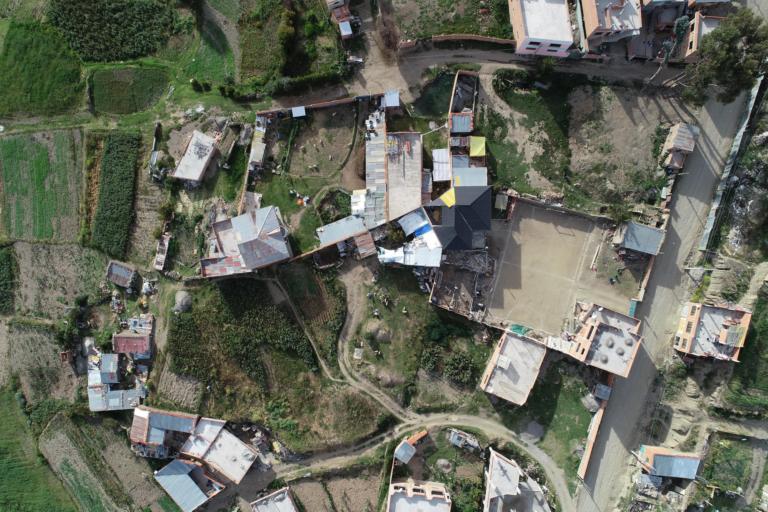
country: BO
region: La Paz
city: La Paz
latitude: -16.5441
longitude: -68.0010
